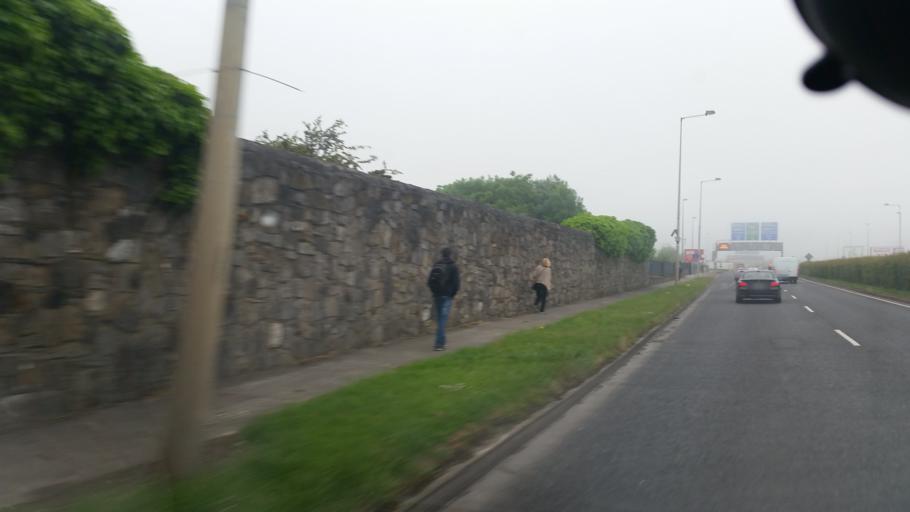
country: IE
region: Leinster
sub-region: Dublin City
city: Finglas
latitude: 53.3992
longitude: -6.3075
